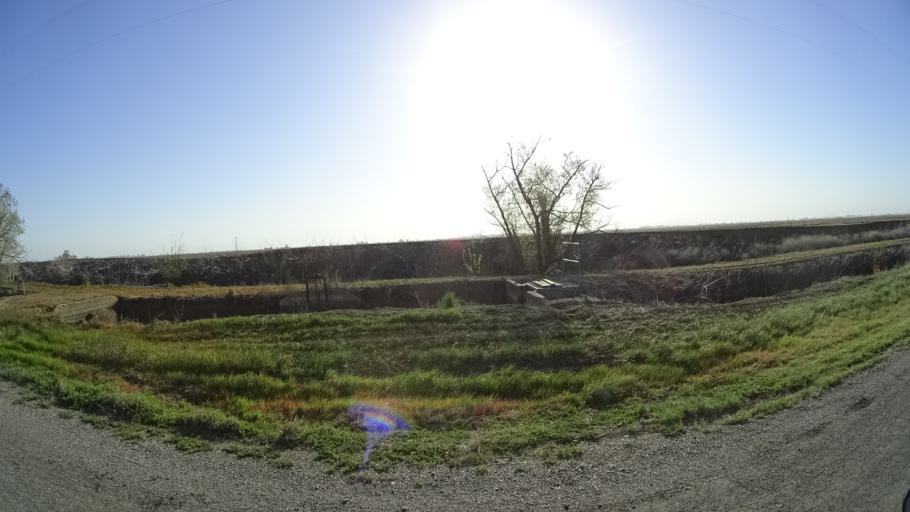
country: US
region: California
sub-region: Colusa County
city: Maxwell
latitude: 39.3997
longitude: -122.2300
